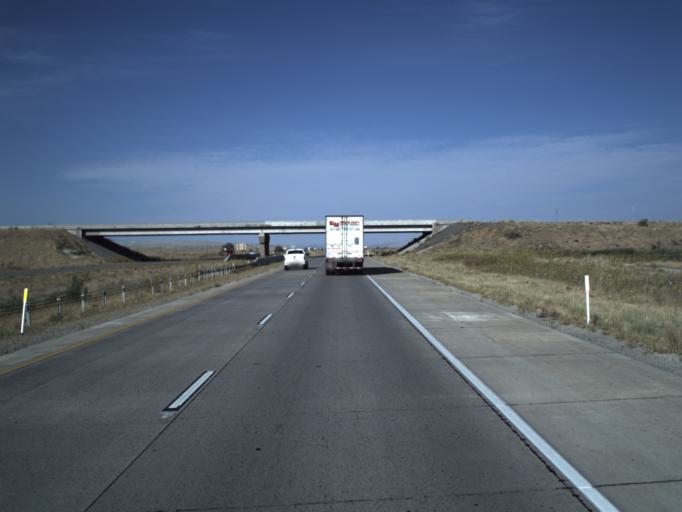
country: US
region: Utah
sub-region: Salt Lake County
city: Magna
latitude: 40.7711
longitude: -112.0608
